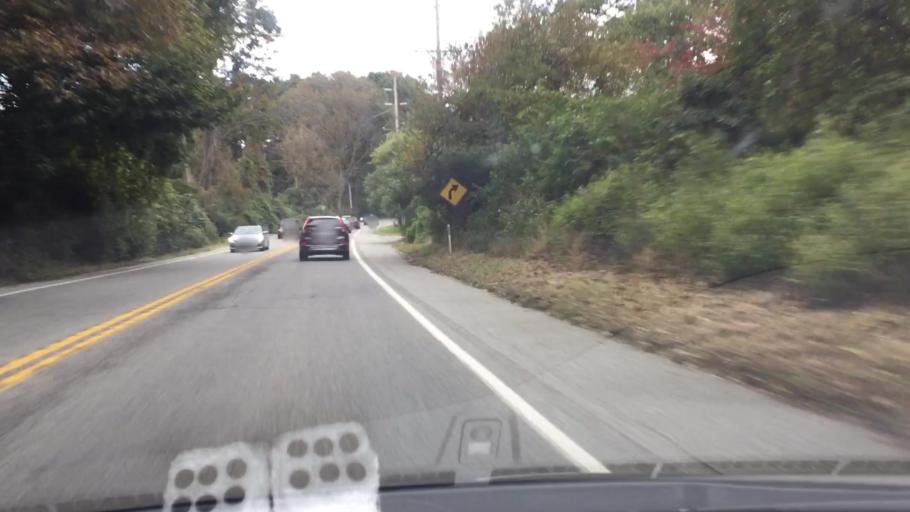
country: US
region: Pennsylvania
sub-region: Delaware County
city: Lima
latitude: 39.9374
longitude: -75.4558
